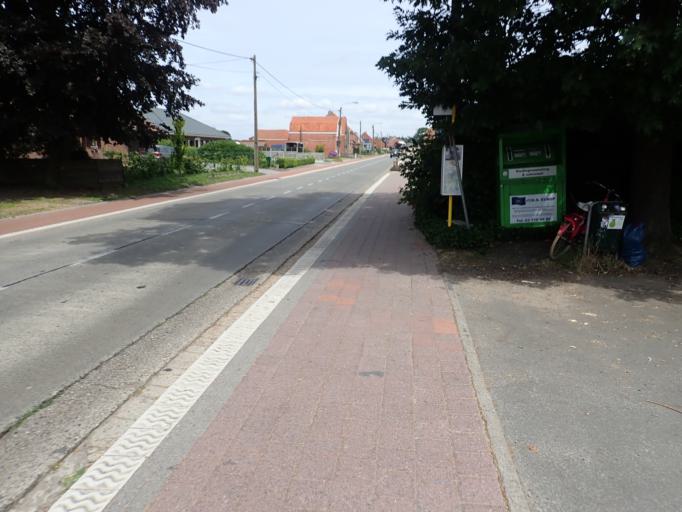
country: BE
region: Flanders
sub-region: Provincie Antwerpen
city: Oostmalle
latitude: 51.3023
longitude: 4.7810
